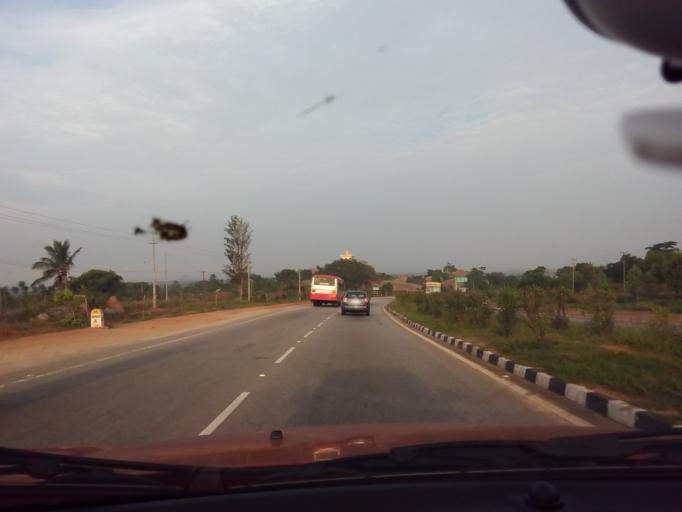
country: IN
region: Karnataka
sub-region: Ramanagara
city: Magadi
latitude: 13.0634
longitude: 77.2796
